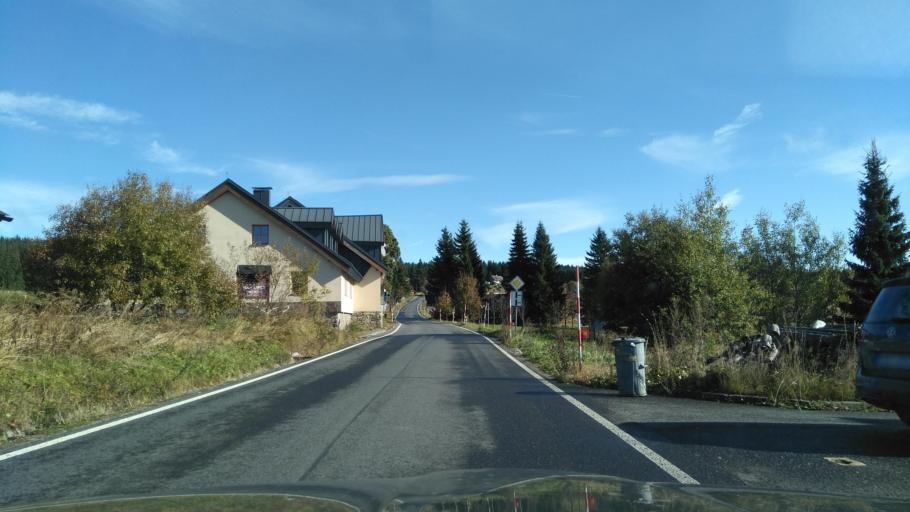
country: CZ
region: Plzensky
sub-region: Okres Klatovy
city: Kasperske Hory
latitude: 49.0280
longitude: 13.5172
